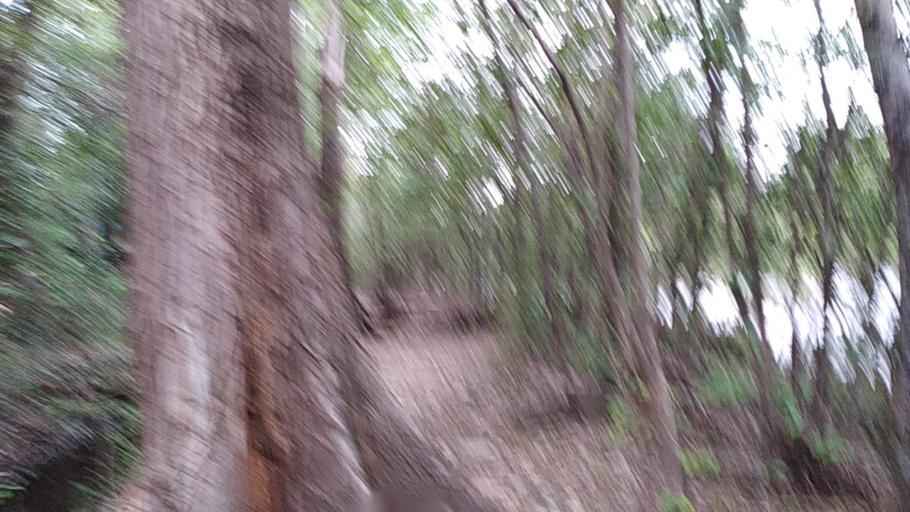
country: AR
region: Cordoba
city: Alta Gracia
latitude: -31.7259
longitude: -64.4377
